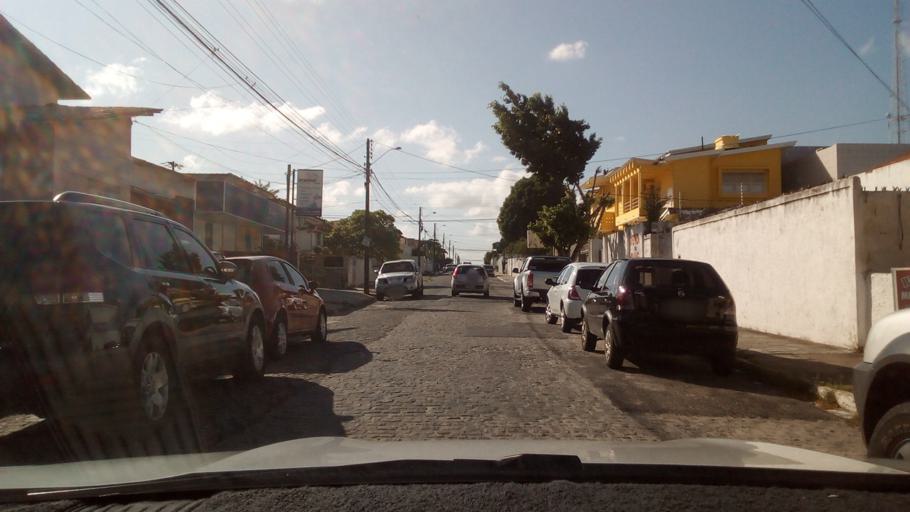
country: BR
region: Paraiba
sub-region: Joao Pessoa
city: Joao Pessoa
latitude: -7.1253
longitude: -34.8761
